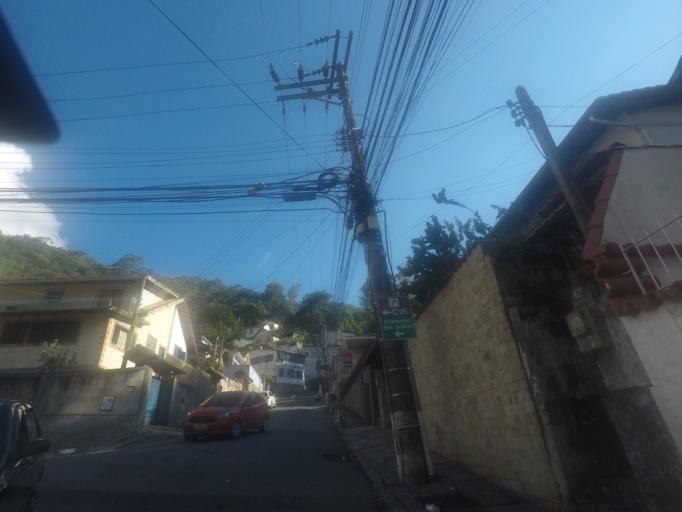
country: BR
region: Rio de Janeiro
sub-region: Petropolis
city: Petropolis
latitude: -22.5069
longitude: -43.1626
